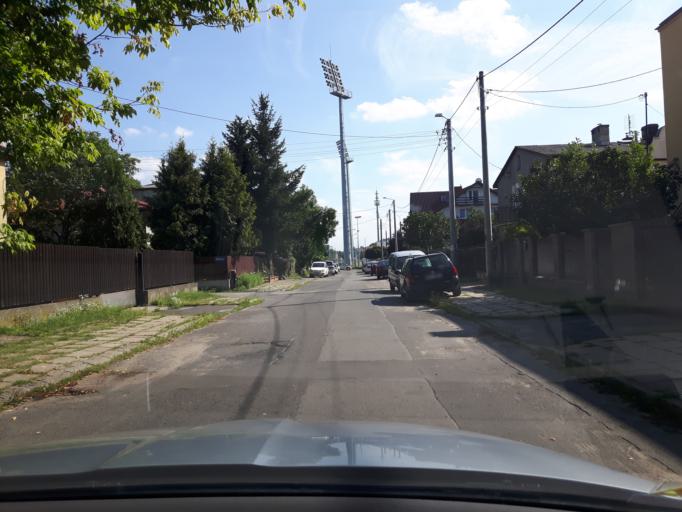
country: PL
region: Masovian Voivodeship
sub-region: Powiat wolominski
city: Zabki
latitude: 52.2942
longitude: 21.1209
